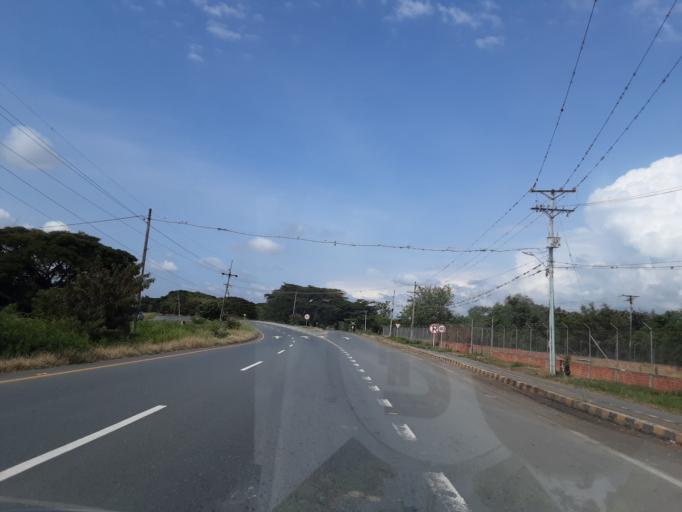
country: CO
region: Valle del Cauca
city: Guacari
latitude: 3.7793
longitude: -76.3253
